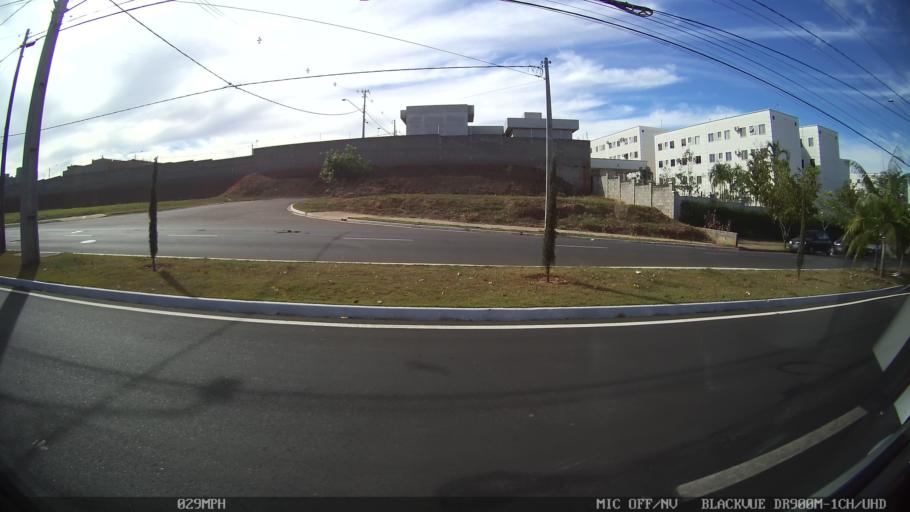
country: BR
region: Sao Paulo
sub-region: Catanduva
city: Catanduva
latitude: -21.1199
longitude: -48.9782
